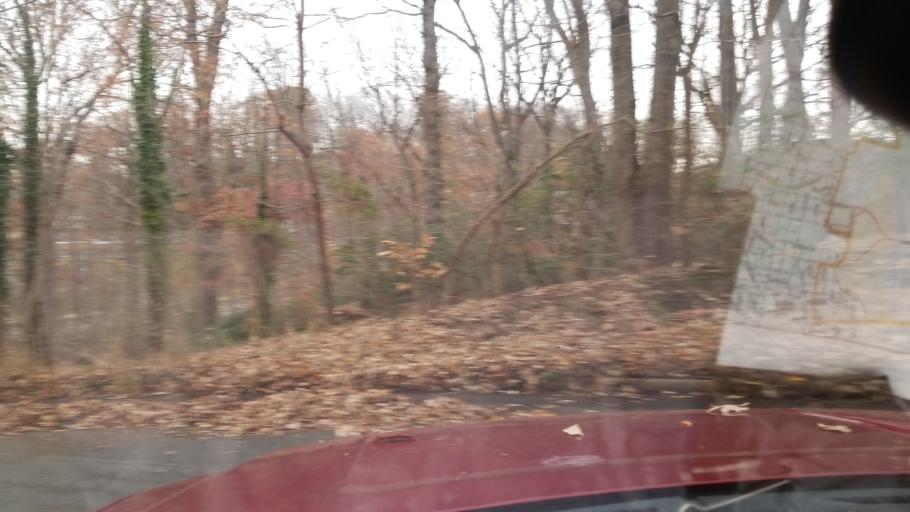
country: US
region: Maryland
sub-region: Prince George's County
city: Silver Hill
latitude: 38.8674
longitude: -76.9585
